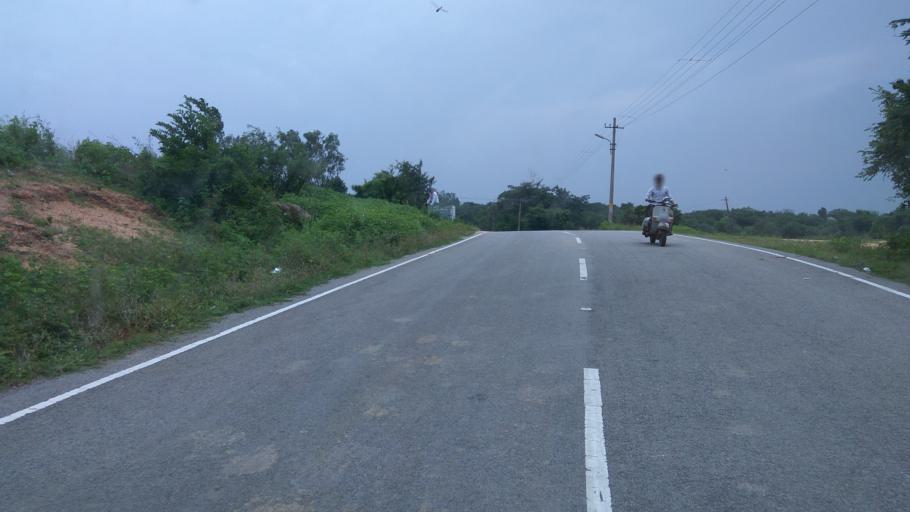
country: IN
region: Telangana
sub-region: Rangareddi
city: Ghatkesar
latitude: 17.5364
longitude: 78.6929
